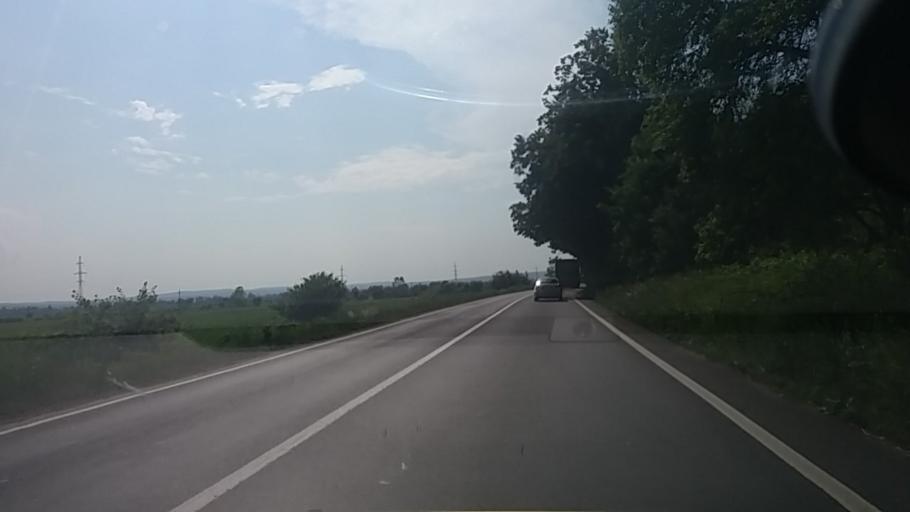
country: RO
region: Arad
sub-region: Comuna Varadia de Mures
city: Varadia de Mures
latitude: 46.0253
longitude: 22.1286
